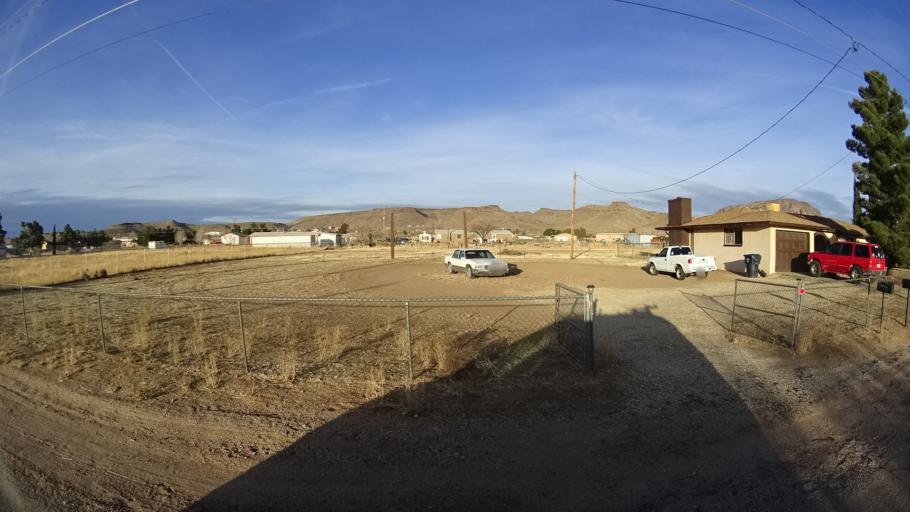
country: US
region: Arizona
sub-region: Mohave County
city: New Kingman-Butler
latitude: 35.2421
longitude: -114.0332
